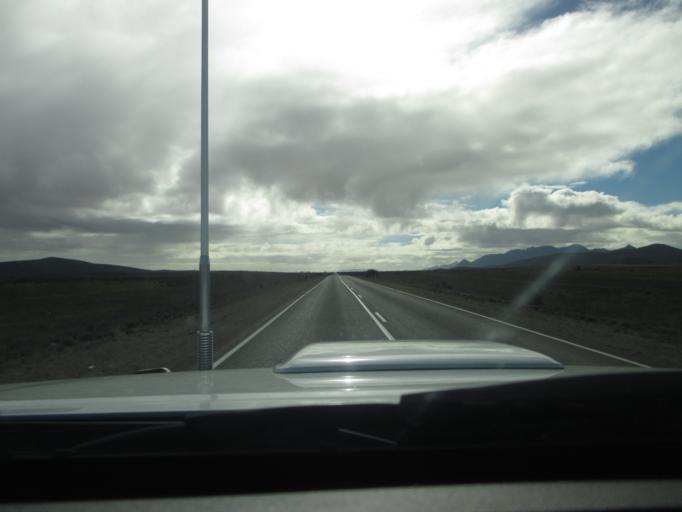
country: AU
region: South Australia
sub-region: Flinders Ranges
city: Quorn
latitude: -31.6513
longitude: 138.3795
